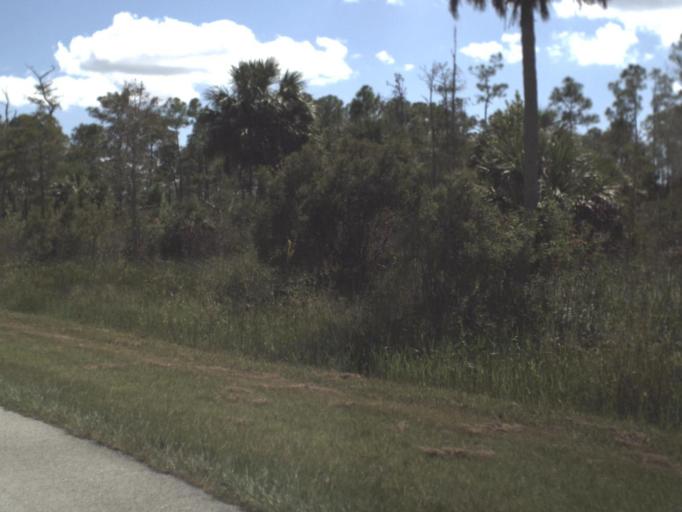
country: US
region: Florida
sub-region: Collier County
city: Lely Resort
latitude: 26.0029
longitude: -81.6050
